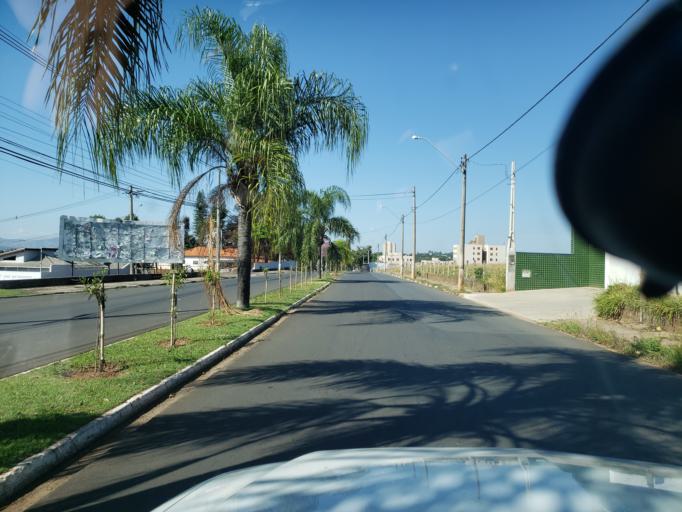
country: BR
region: Sao Paulo
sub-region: Itapira
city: Itapira
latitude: -22.4217
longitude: -46.8386
